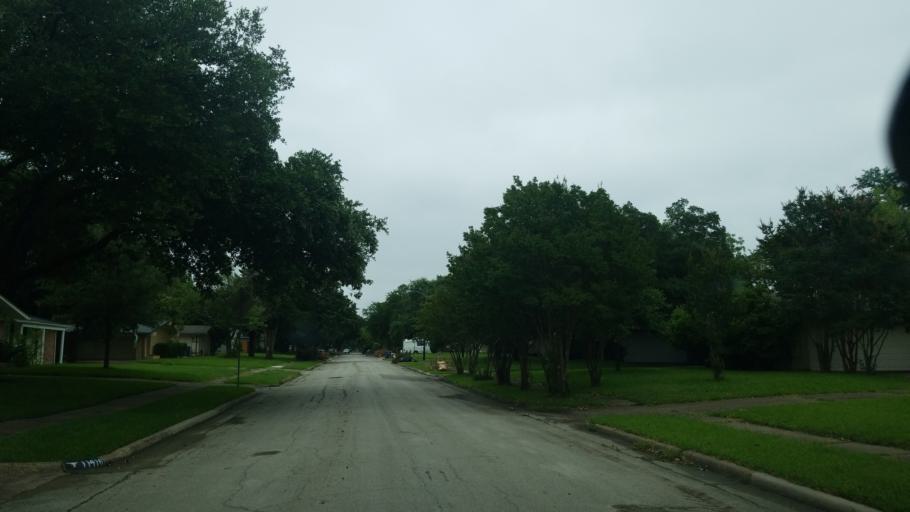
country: US
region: Texas
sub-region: Dallas County
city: Farmers Branch
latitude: 32.9029
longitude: -96.8693
